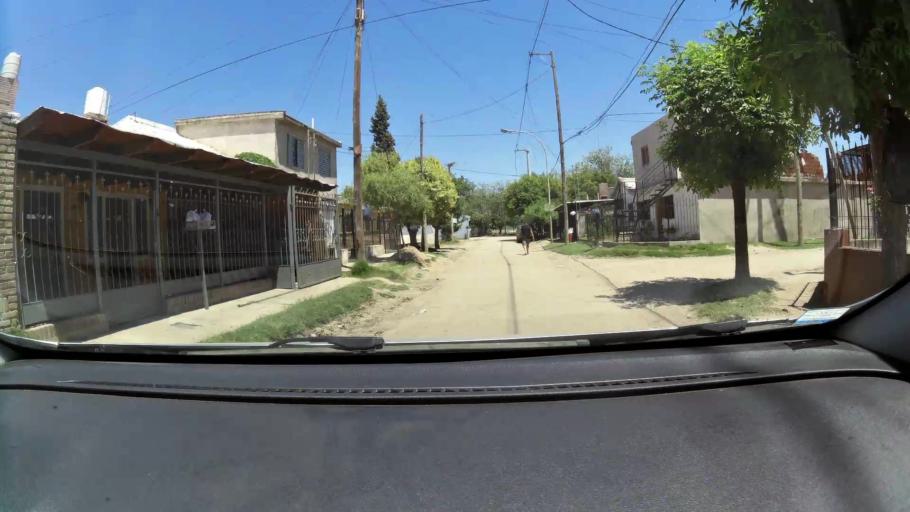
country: AR
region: Cordoba
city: Malvinas Argentinas
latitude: -31.4279
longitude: -64.1124
